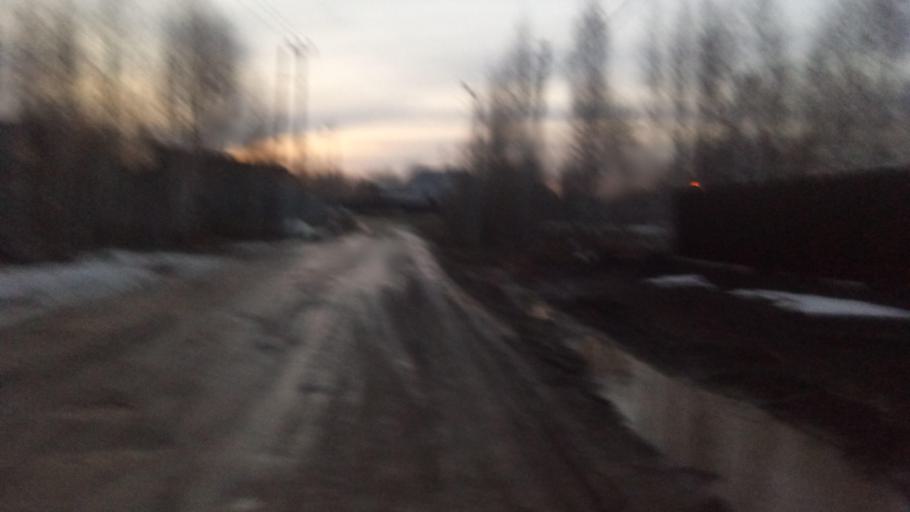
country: RU
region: Chelyabinsk
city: Sargazy
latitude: 55.1026
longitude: 61.2045
